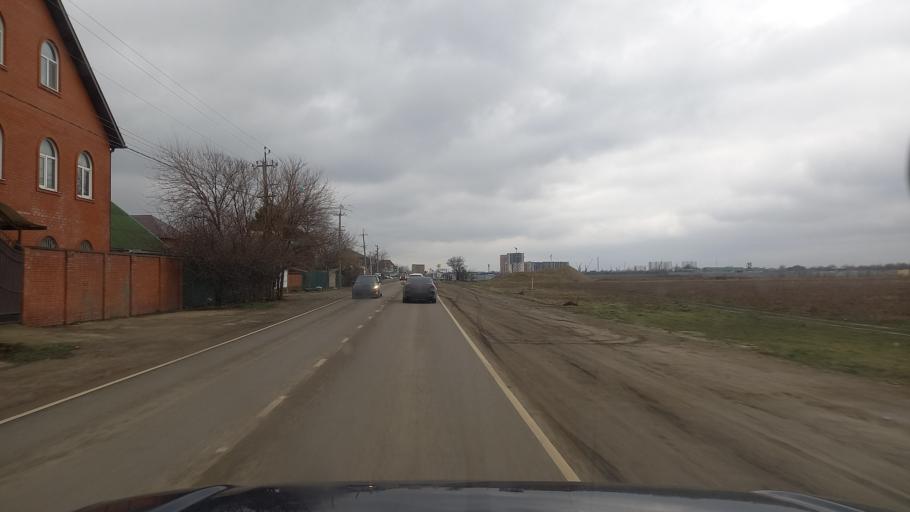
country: RU
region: Krasnodarskiy
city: Pashkovskiy
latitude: 45.0592
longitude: 39.1635
